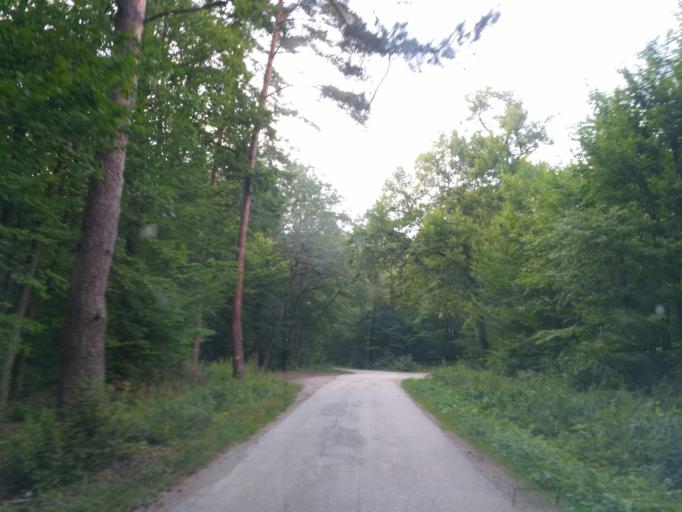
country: SK
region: Kosicky
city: Kosice
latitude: 48.7305
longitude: 21.1809
